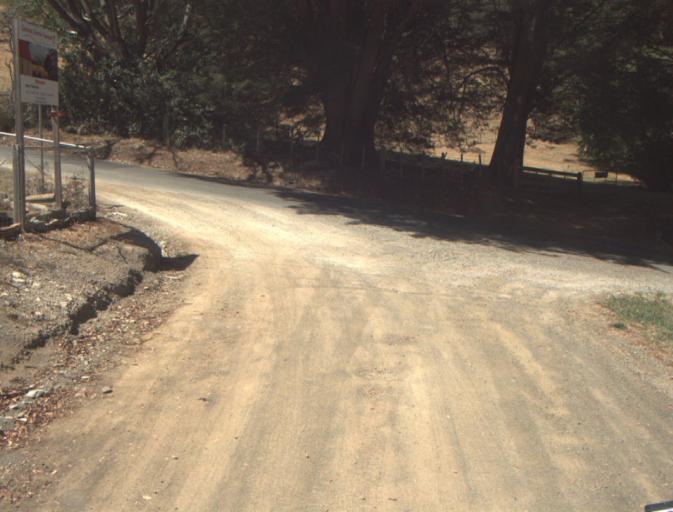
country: AU
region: Tasmania
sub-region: Launceston
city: Mayfield
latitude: -41.2582
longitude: 147.1882
